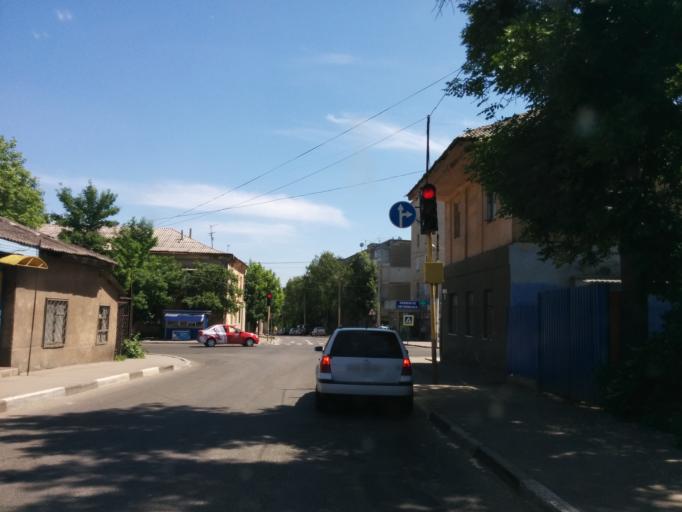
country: MD
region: Raionul Soroca
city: Soroca
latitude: 48.1620
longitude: 28.3009
